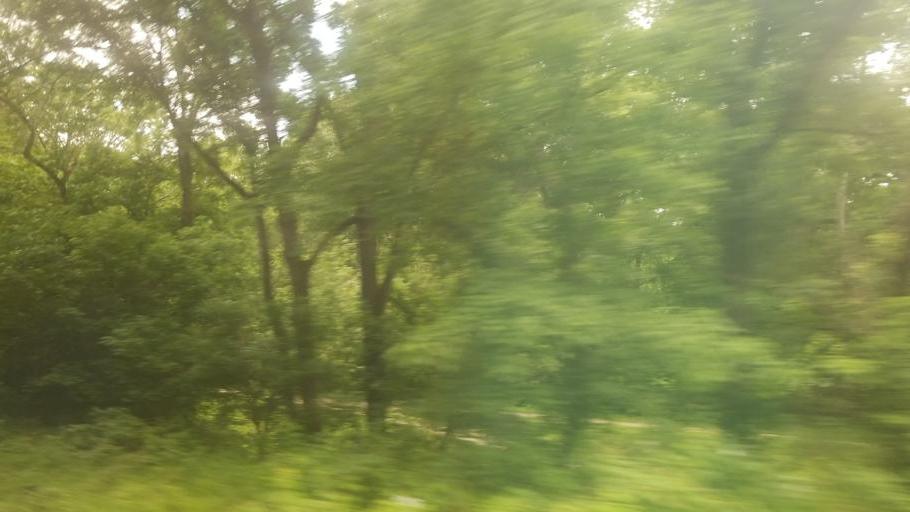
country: US
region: Maryland
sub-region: Frederick County
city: Point of Rocks
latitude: 39.3114
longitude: -77.5676
